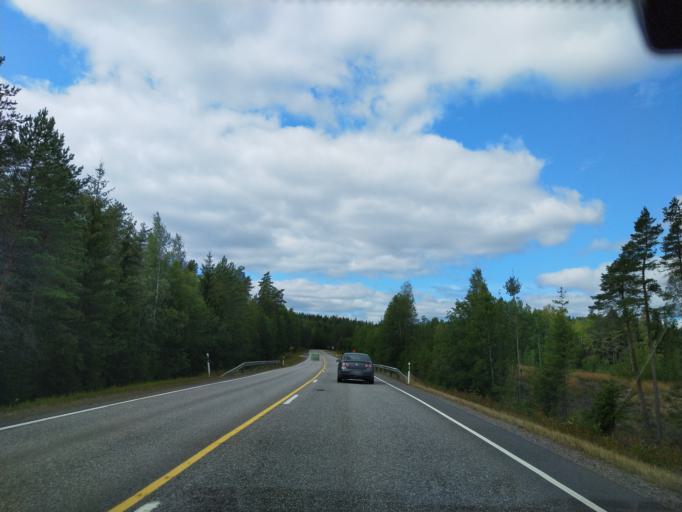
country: FI
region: Haeme
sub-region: Riihimaeki
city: Loppi
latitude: 60.7374
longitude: 24.3751
